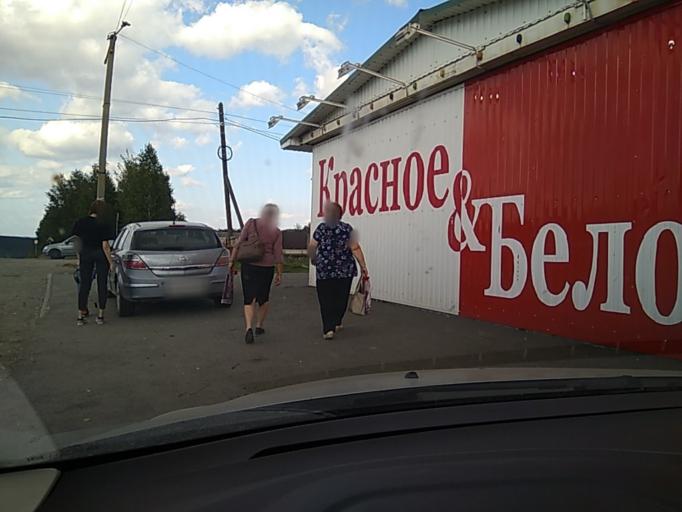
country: RU
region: Chelyabinsk
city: Karabash
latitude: 55.4895
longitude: 60.2406
